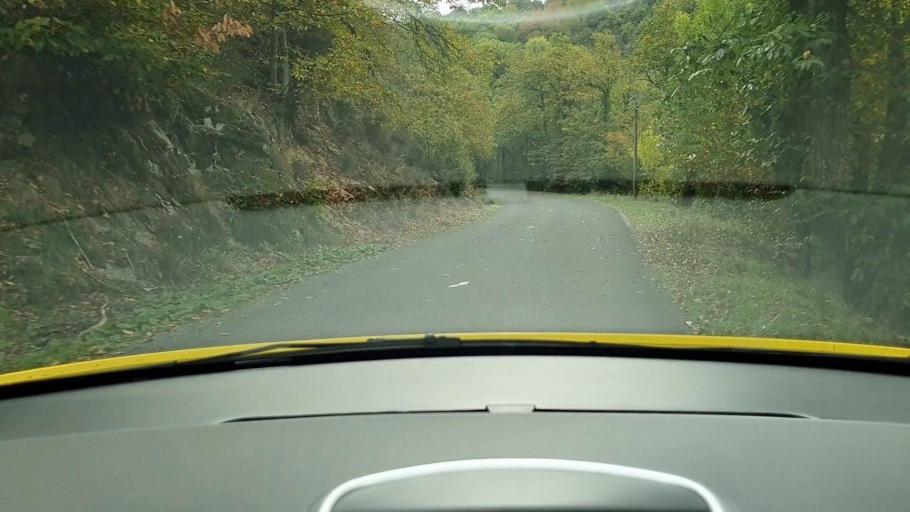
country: FR
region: Languedoc-Roussillon
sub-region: Departement de la Lozere
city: Meyrueis
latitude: 44.0625
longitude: 3.4330
